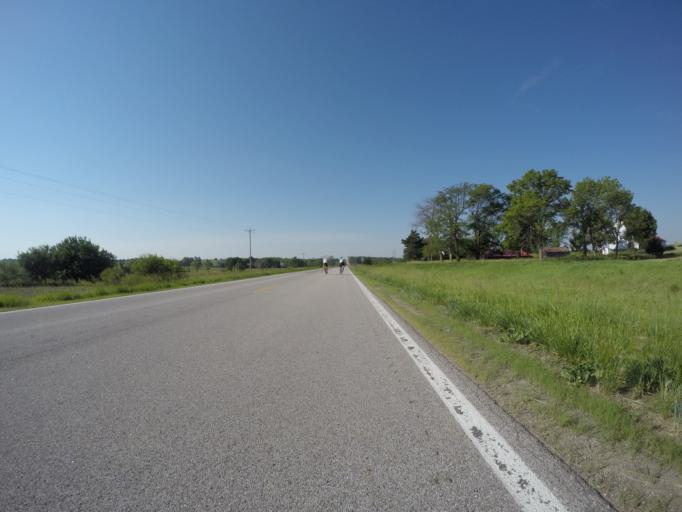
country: US
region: Nebraska
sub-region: Gage County
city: Wymore
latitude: 40.0478
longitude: -96.4828
